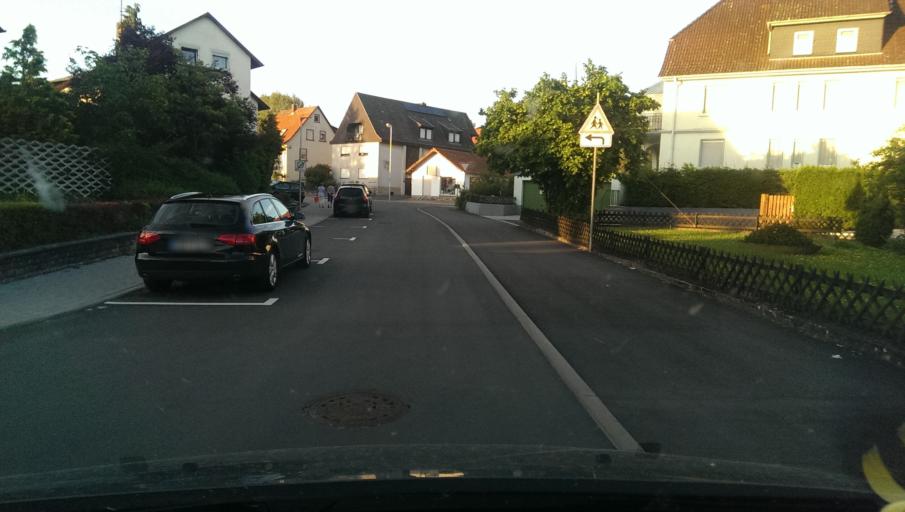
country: DE
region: Baden-Wuerttemberg
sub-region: Regierungsbezirk Stuttgart
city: Tauberbischofsheim
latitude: 49.6247
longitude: 9.6695
